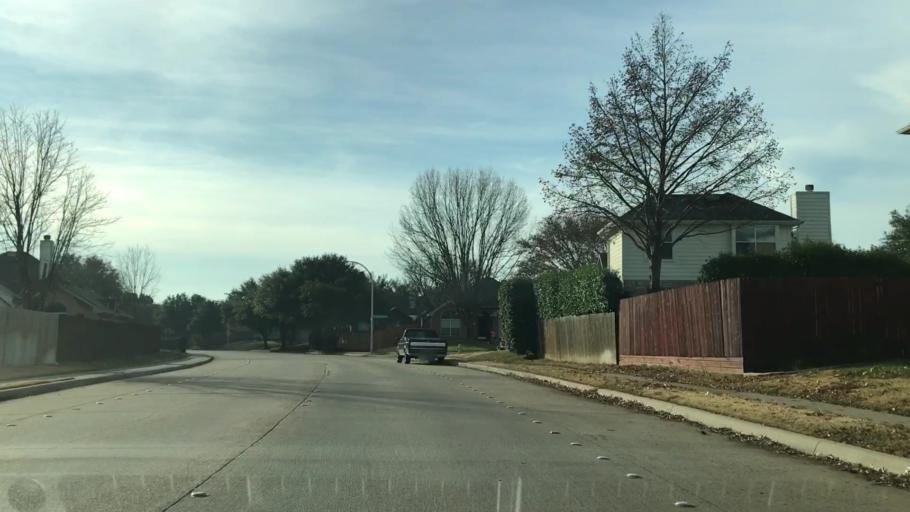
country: US
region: Texas
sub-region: Tarrant County
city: Watauga
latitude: 32.8763
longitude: -97.2799
